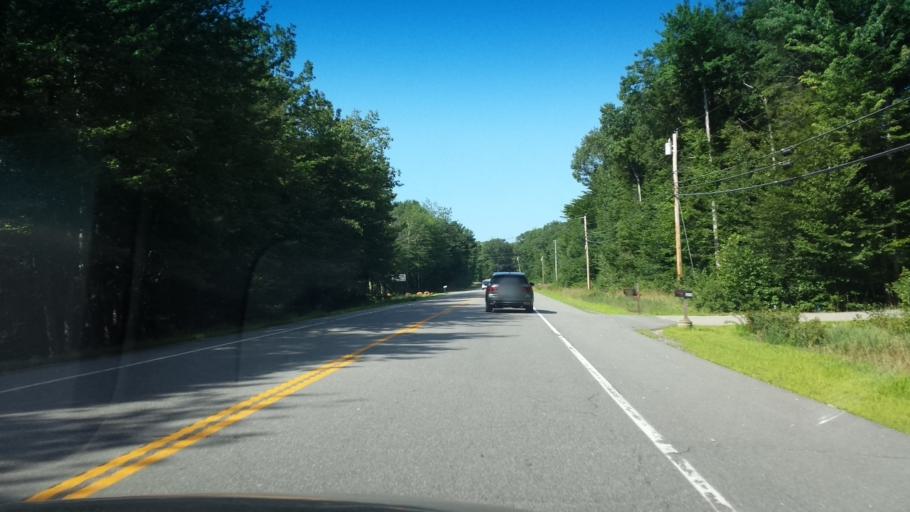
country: US
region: Maine
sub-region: York County
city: Sanford (historical)
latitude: 43.4297
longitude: -70.8058
